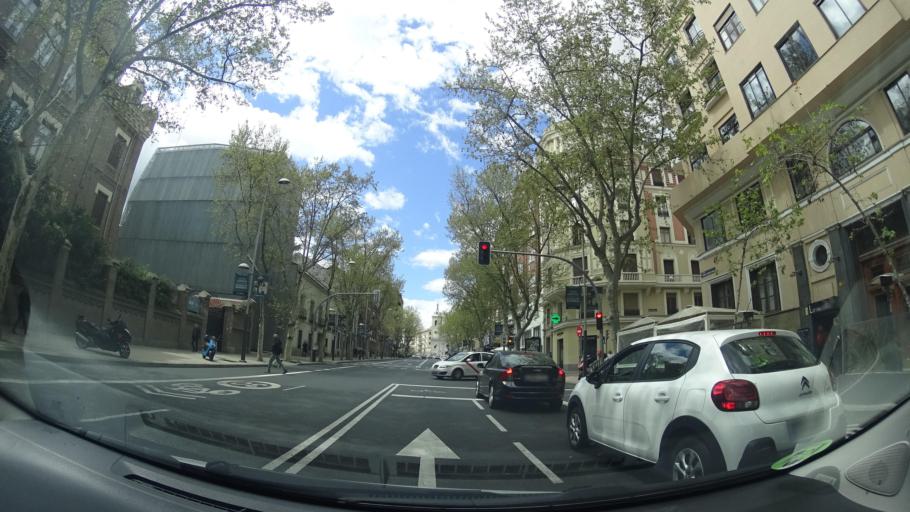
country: ES
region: Madrid
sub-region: Provincia de Madrid
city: Chamberi
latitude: 40.4347
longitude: -3.6958
